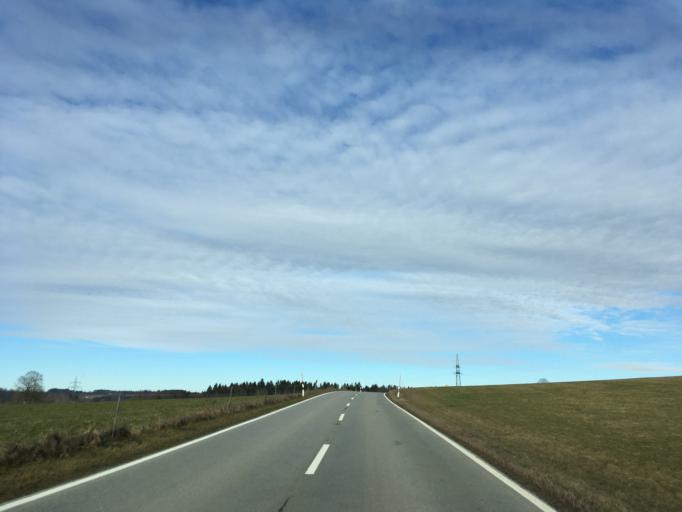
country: DE
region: Bavaria
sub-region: Upper Bavaria
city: Gars
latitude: 48.1631
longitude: 12.2713
